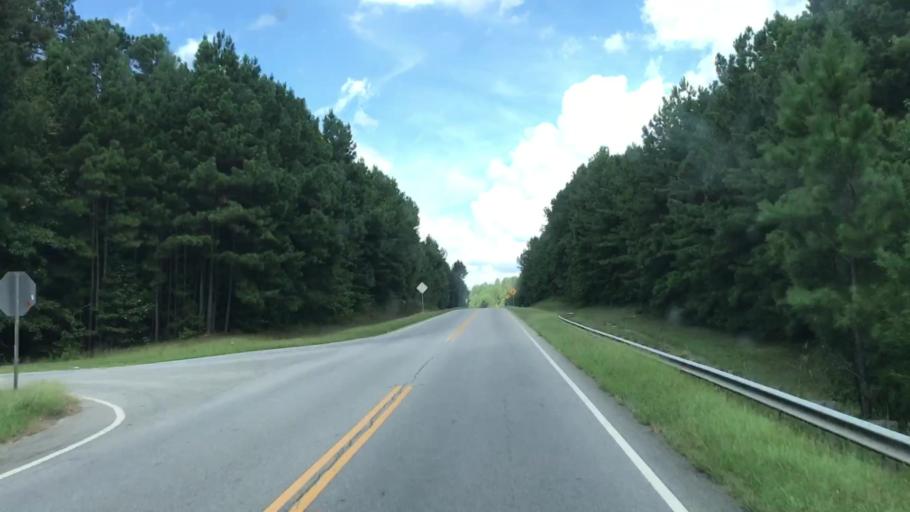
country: US
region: Georgia
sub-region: Greene County
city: Greensboro
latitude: 33.7111
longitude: -83.2917
